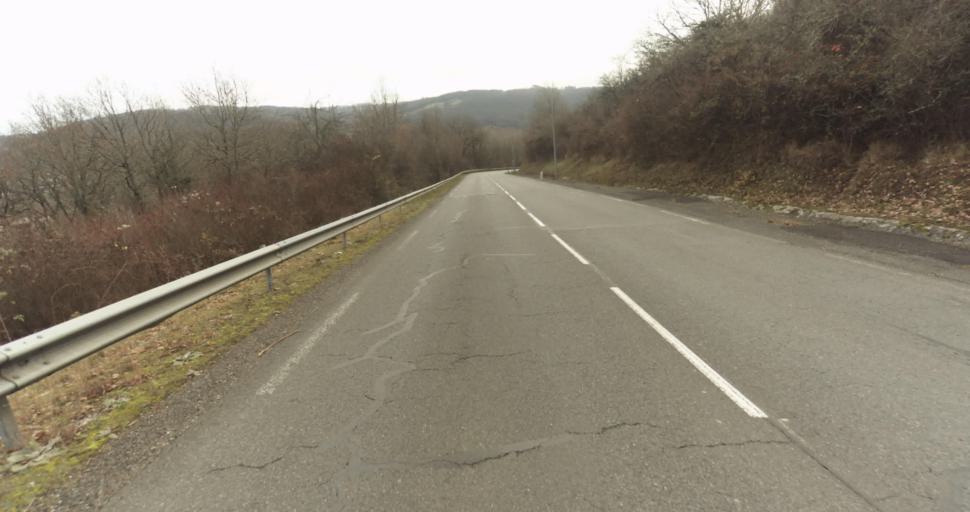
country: FR
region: Midi-Pyrenees
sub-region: Departement du Lot
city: Figeac
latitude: 44.6112
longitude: 2.0139
